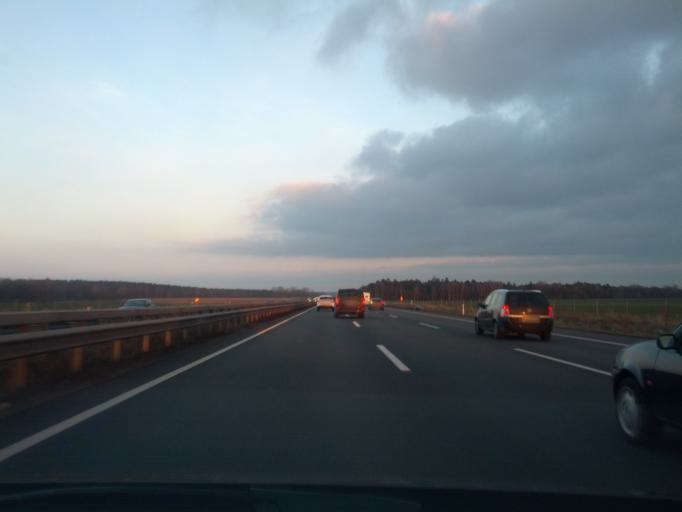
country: DE
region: Lower Saxony
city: Kalbe
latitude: 53.3090
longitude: 9.5553
